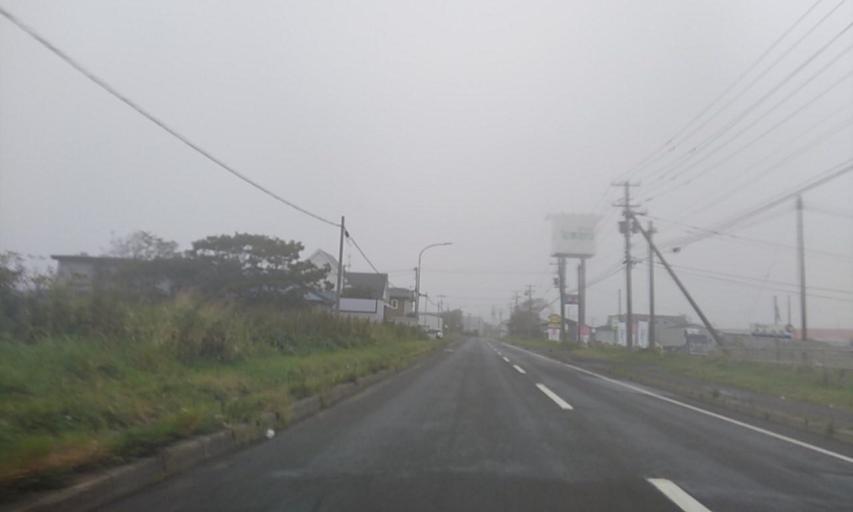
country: JP
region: Hokkaido
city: Nemuro
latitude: 43.3139
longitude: 145.5991
